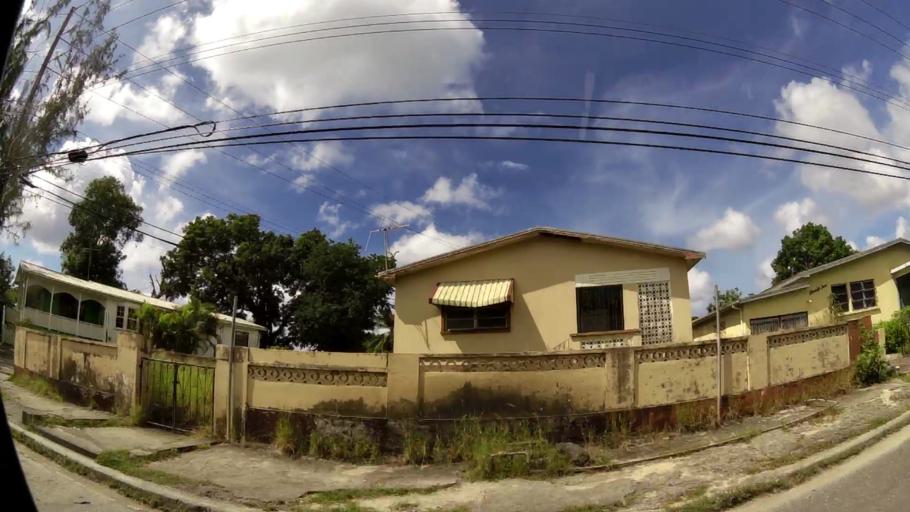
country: BB
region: Saint Michael
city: Bridgetown
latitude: 13.1272
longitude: -59.6249
